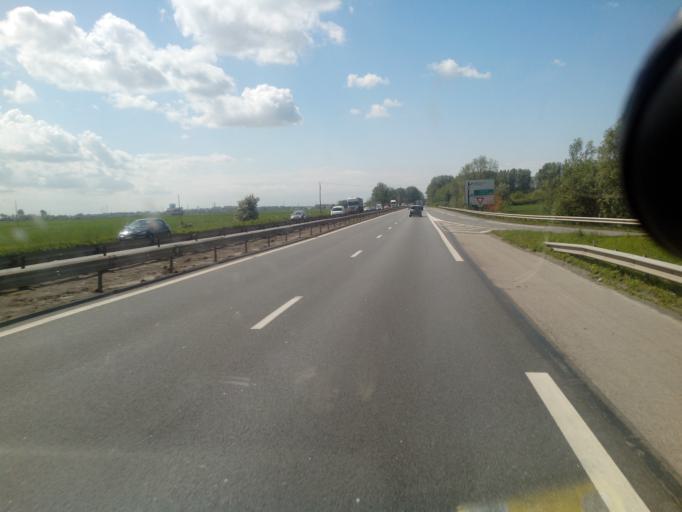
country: FR
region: Nord-Pas-de-Calais
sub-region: Departement du Nord
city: Cappelle-la-Grande
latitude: 50.9902
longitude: 2.3503
